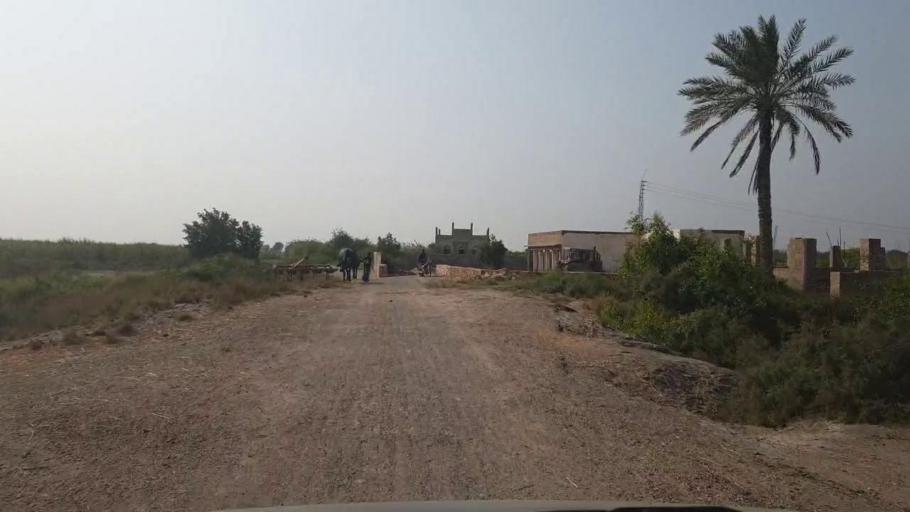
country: PK
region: Sindh
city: Bulri
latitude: 25.0457
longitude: 68.3651
